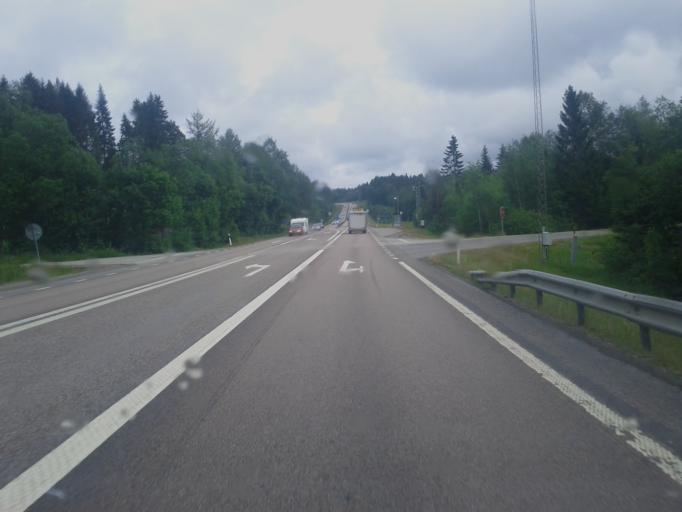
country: SE
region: Vaesternorrland
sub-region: Timra Kommun
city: Soraker
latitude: 62.5617
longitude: 17.7093
